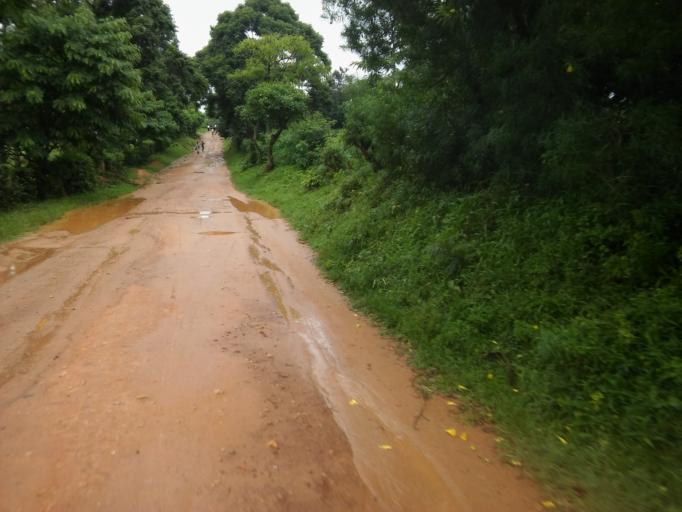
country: UG
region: Eastern Region
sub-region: Mbale District
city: Mbale
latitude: 0.9858
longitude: 34.2171
